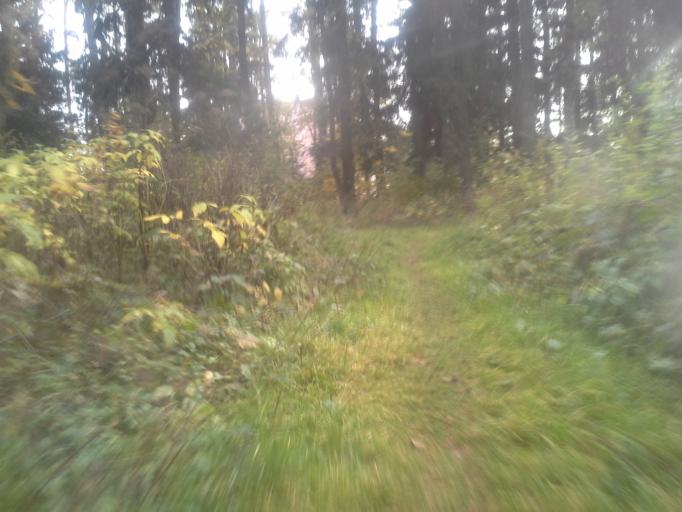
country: RU
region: Moskovskaya
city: Selyatino
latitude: 55.4668
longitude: 36.9457
